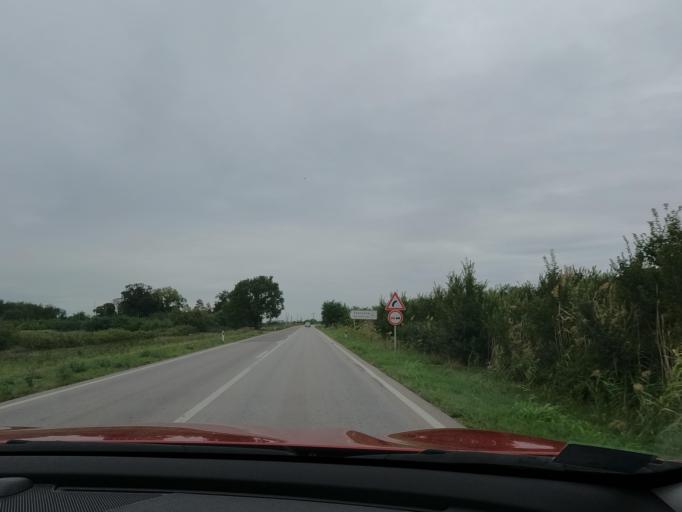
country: RS
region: Autonomna Pokrajina Vojvodina
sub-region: Severnobanatski Okrug
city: Kikinda
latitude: 45.7656
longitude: 20.4232
